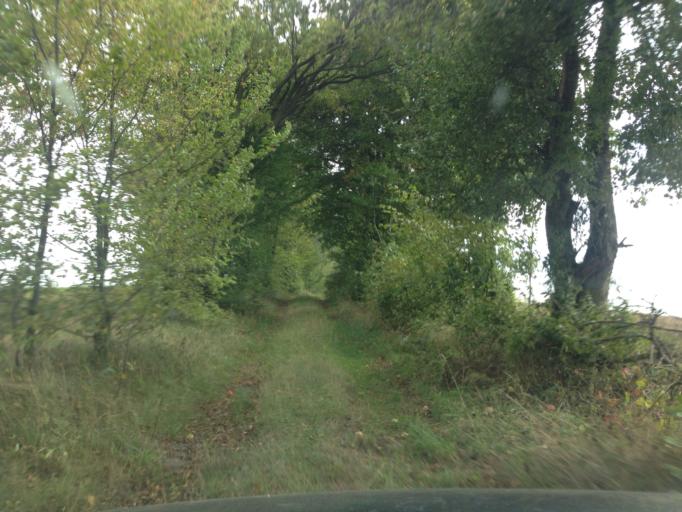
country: PL
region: Warmian-Masurian Voivodeship
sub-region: Powiat dzialdowski
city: Lidzbark
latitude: 53.2596
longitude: 19.7614
